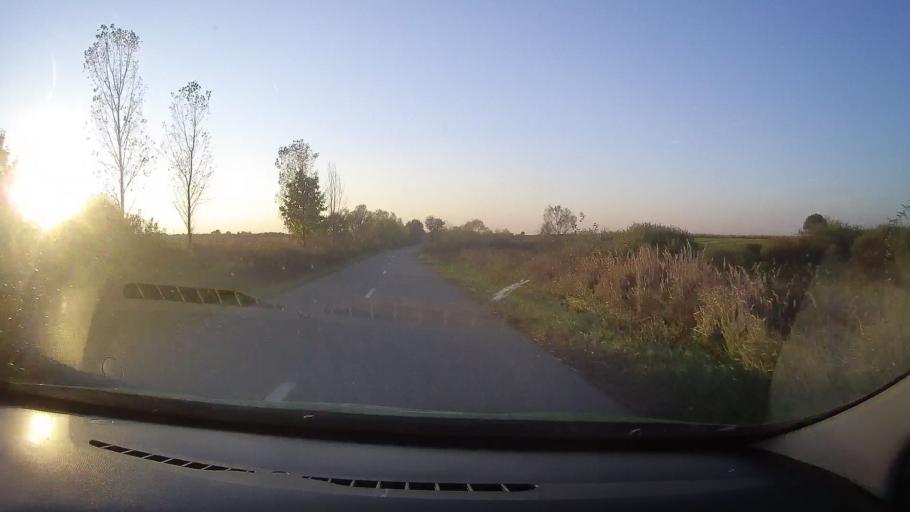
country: RO
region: Timis
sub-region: Comuna Traian Vuia
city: Traian Vuia
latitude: 45.7844
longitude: 22.0438
